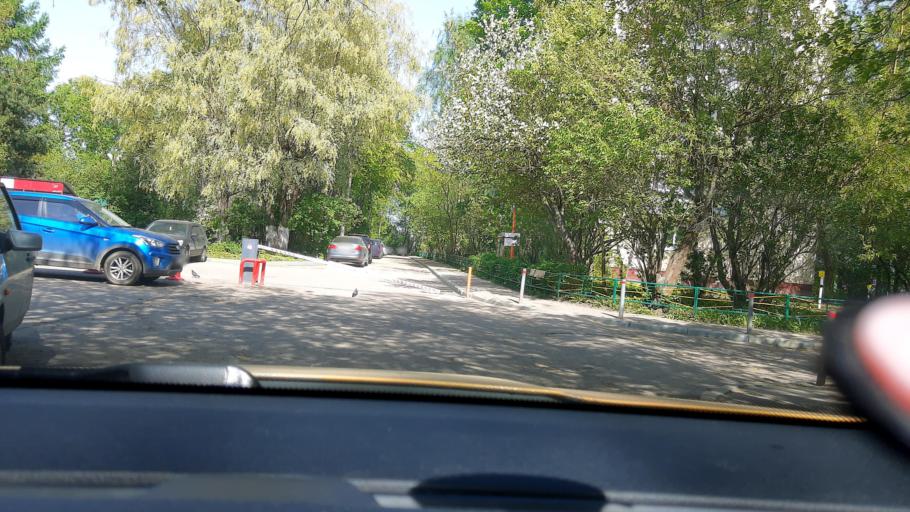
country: RU
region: Moskovskaya
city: Novopodrezkovo
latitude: 55.9532
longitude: 37.3329
